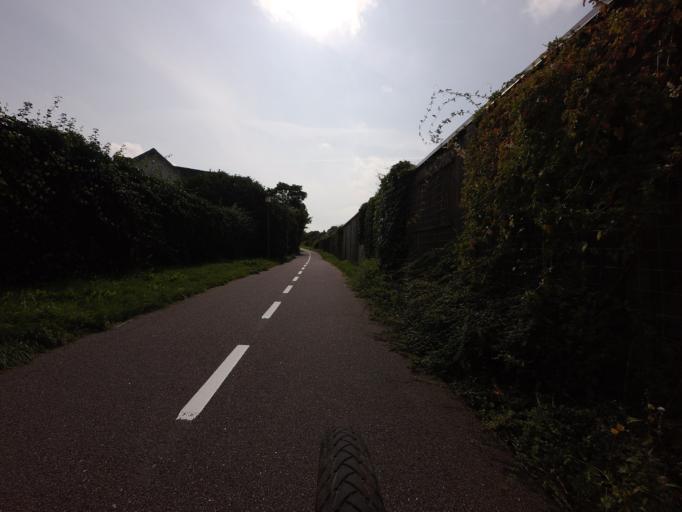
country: DK
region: Zealand
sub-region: Naestved Kommune
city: Naestved
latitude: 55.2270
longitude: 11.7728
